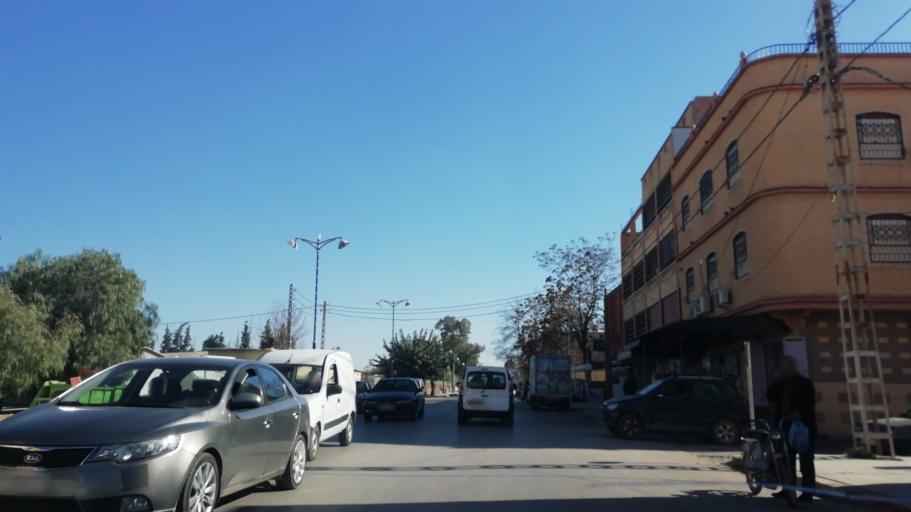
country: DZ
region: Tlemcen
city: Nedroma
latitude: 34.8445
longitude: -1.7207
